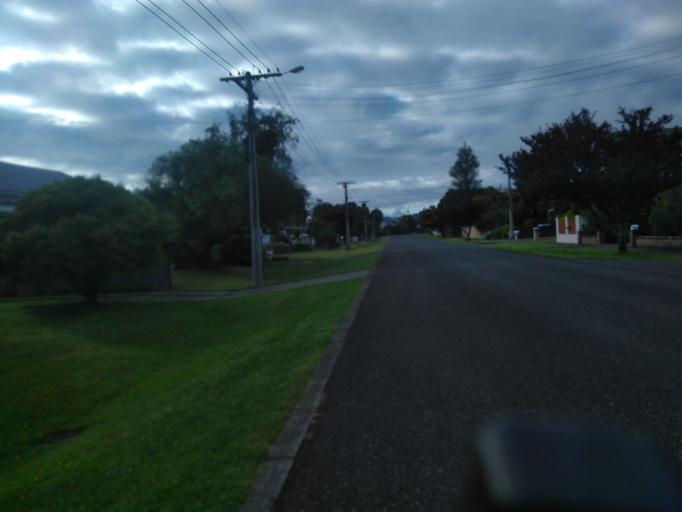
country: NZ
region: Gisborne
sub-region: Gisborne District
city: Gisborne
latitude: -38.6591
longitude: 178.0305
